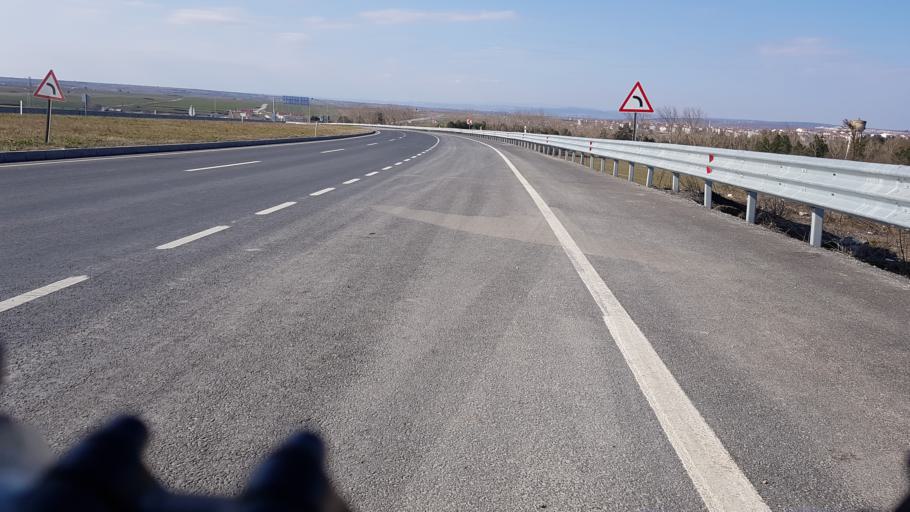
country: TR
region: Tekirdag
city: Saray
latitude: 41.4185
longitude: 27.9214
